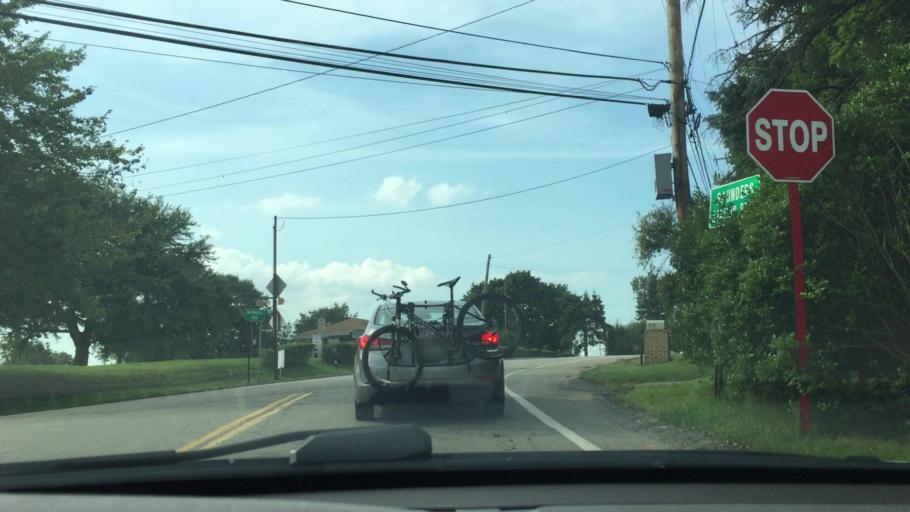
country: US
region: Pennsylvania
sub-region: Allegheny County
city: Pitcairn
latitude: 40.4224
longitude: -79.7495
